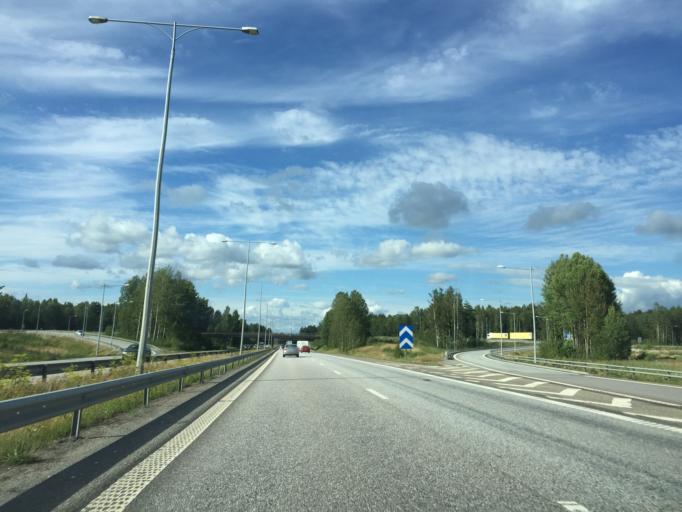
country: SE
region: OErebro
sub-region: Orebro Kommun
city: Orebro
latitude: 59.2368
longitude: 15.1450
